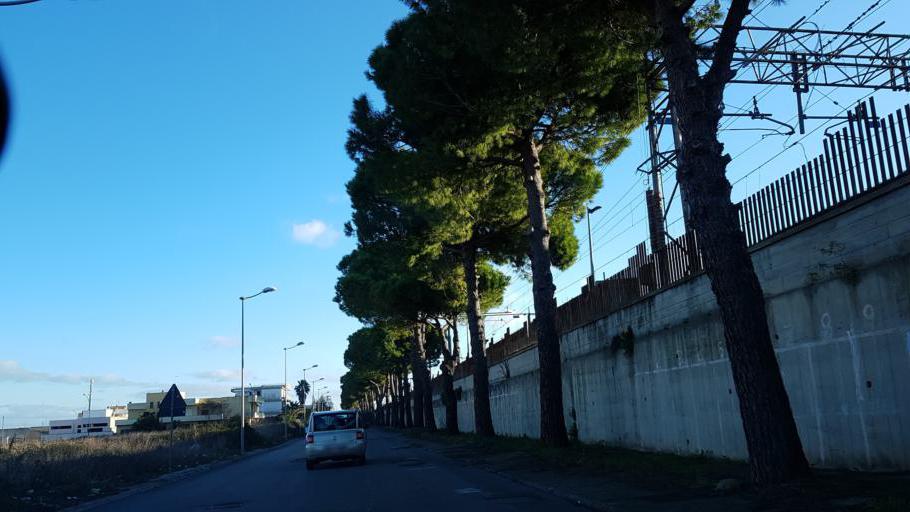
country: IT
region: Apulia
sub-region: Provincia di Lecce
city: Squinzano
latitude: 40.4377
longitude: 18.0480
